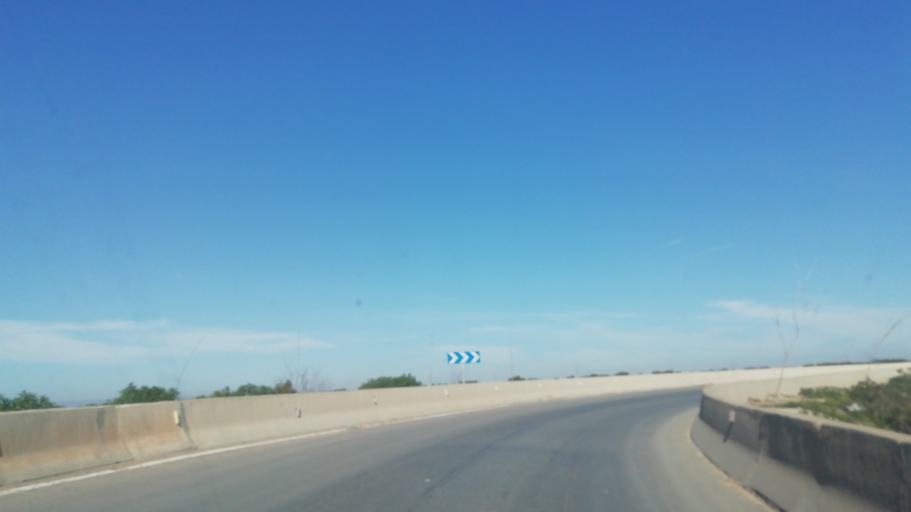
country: DZ
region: Oran
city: Es Senia
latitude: 35.6003
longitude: -0.5758
